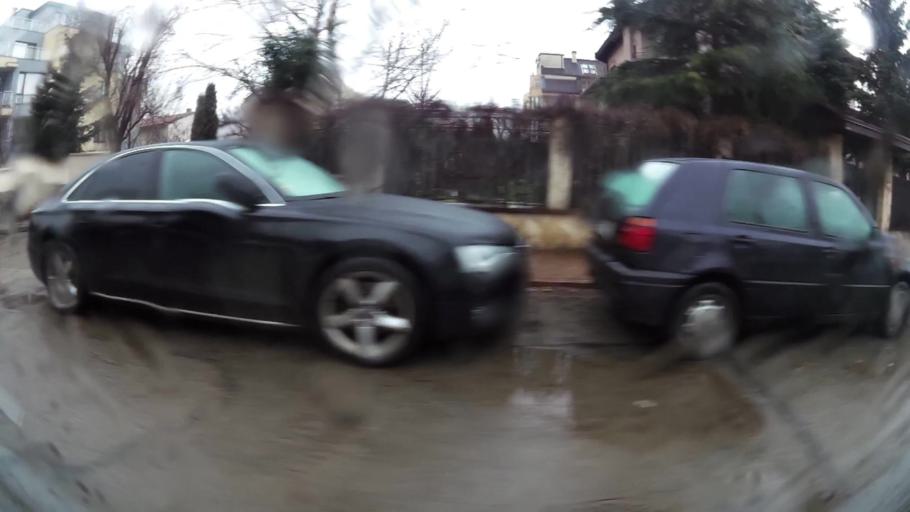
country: BG
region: Sofia-Capital
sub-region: Stolichna Obshtina
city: Sofia
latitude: 42.6487
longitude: 23.3310
